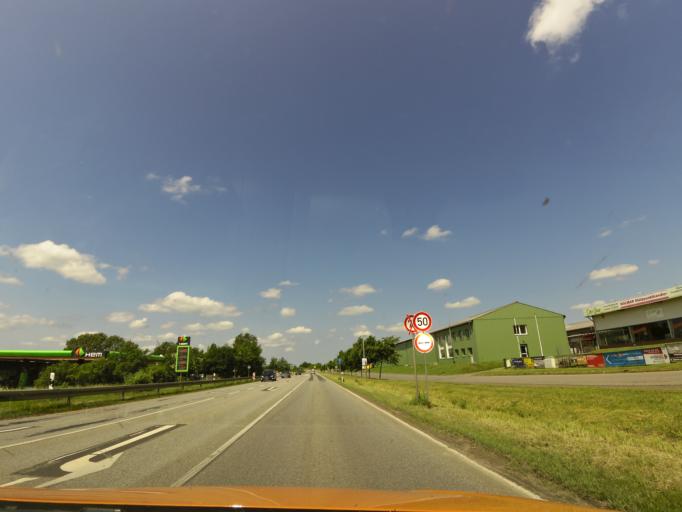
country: DE
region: Mecklenburg-Vorpommern
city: Gadebusch
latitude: 53.6846
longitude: 11.1356
